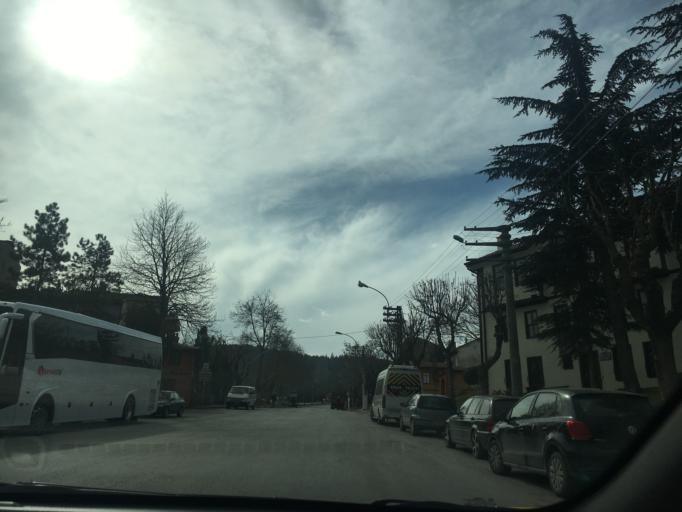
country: TR
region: Eskisehir
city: Eskisehir
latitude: 39.7624
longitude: 30.5249
